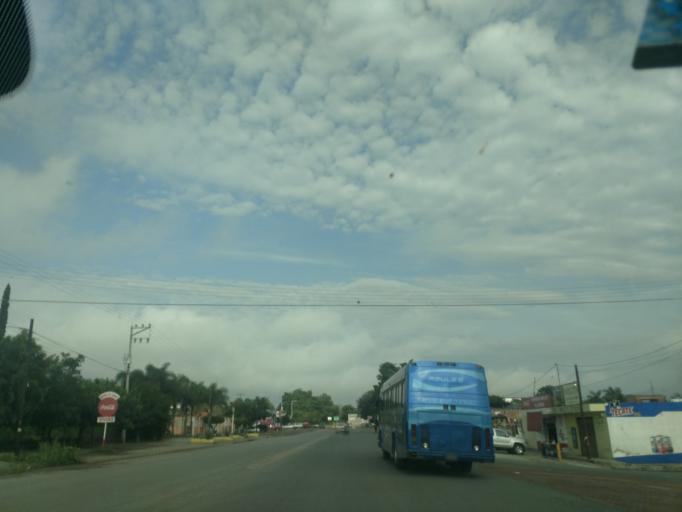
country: MX
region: Jalisco
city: Ameca
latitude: 20.5381
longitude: -104.0435
